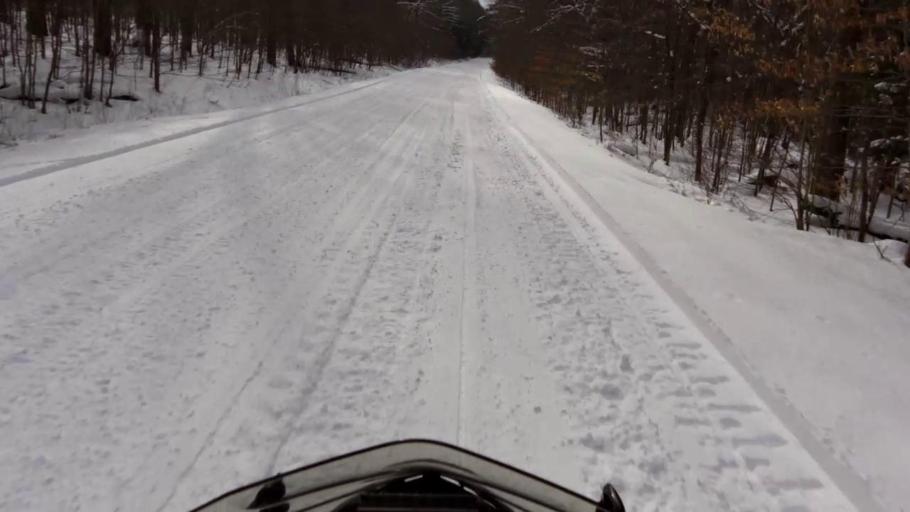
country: US
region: New York
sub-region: Cattaraugus County
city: Salamanca
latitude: 42.0821
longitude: -78.7487
